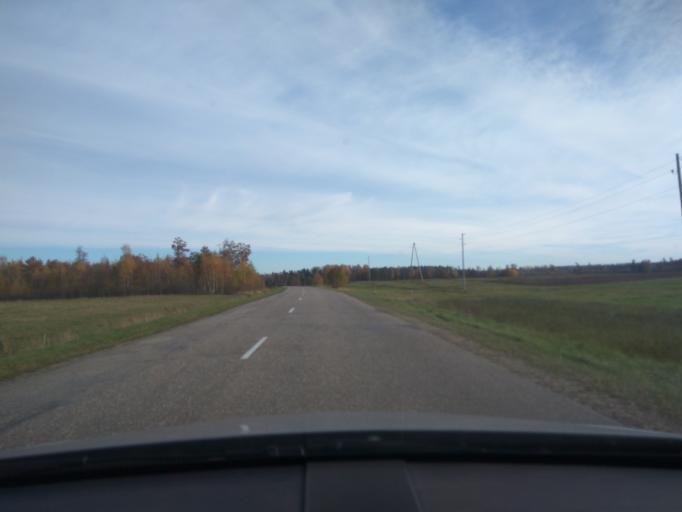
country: LV
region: Alsunga
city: Alsunga
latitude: 56.9885
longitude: 21.5986
